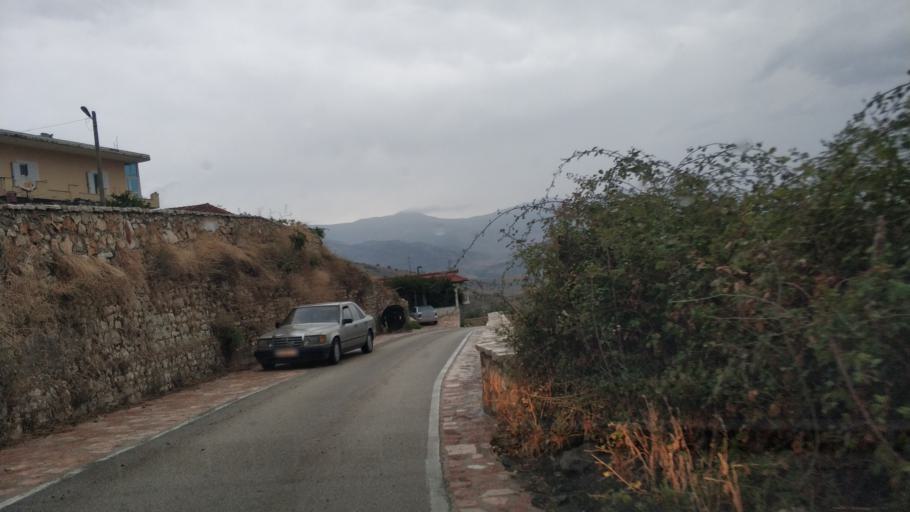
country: AL
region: Vlore
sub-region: Rrethi i Sarandes
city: Lukove
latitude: 39.9438
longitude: 19.9692
